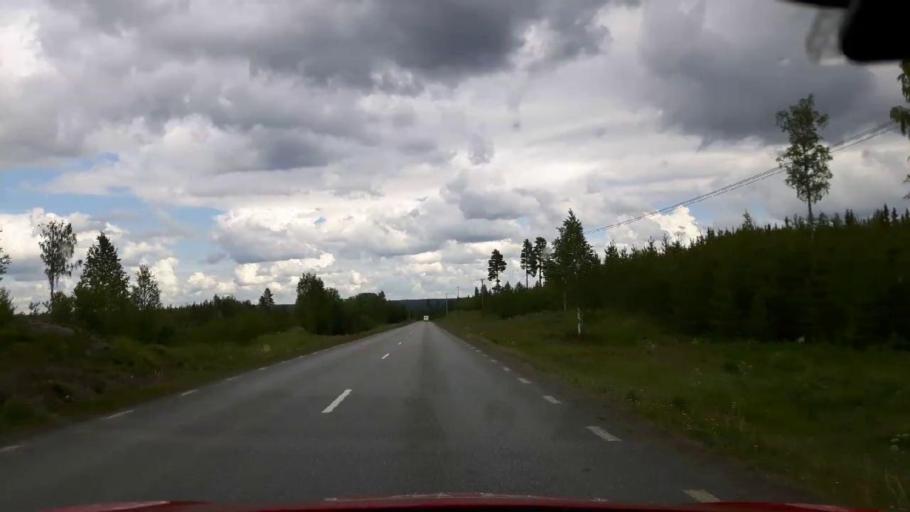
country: SE
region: Jaemtland
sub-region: Krokoms Kommun
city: Krokom
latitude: 63.5409
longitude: 14.2638
